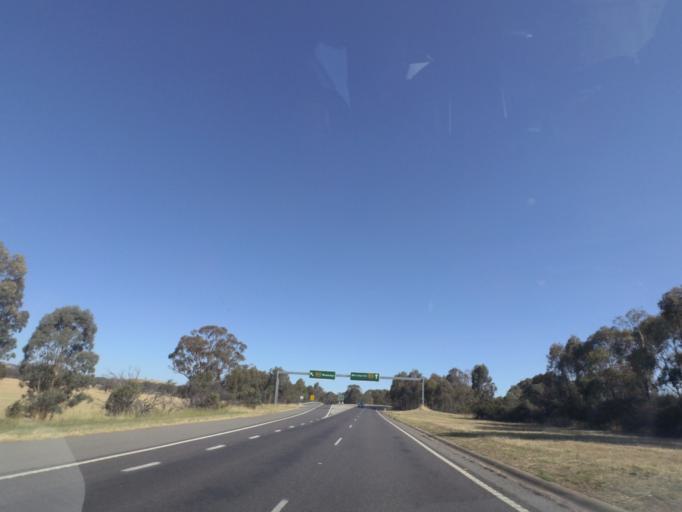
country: AU
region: Victoria
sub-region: Murrindindi
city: Kinglake West
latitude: -36.9803
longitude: 145.1449
